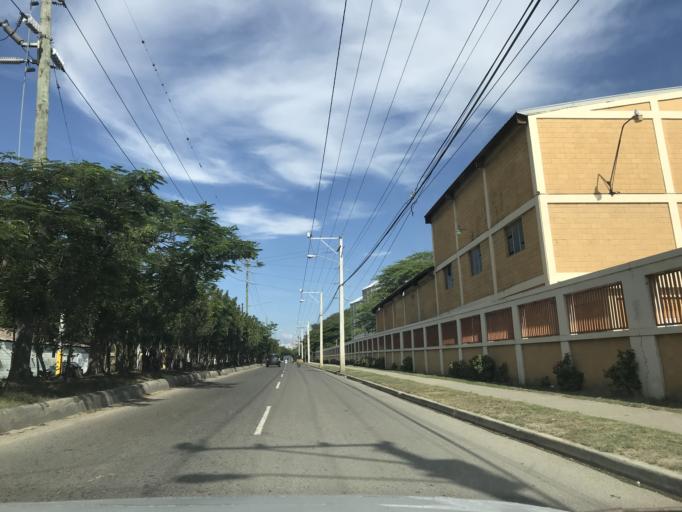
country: DO
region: Santiago
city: Santiago de los Caballeros
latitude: 19.4431
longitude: -70.7377
